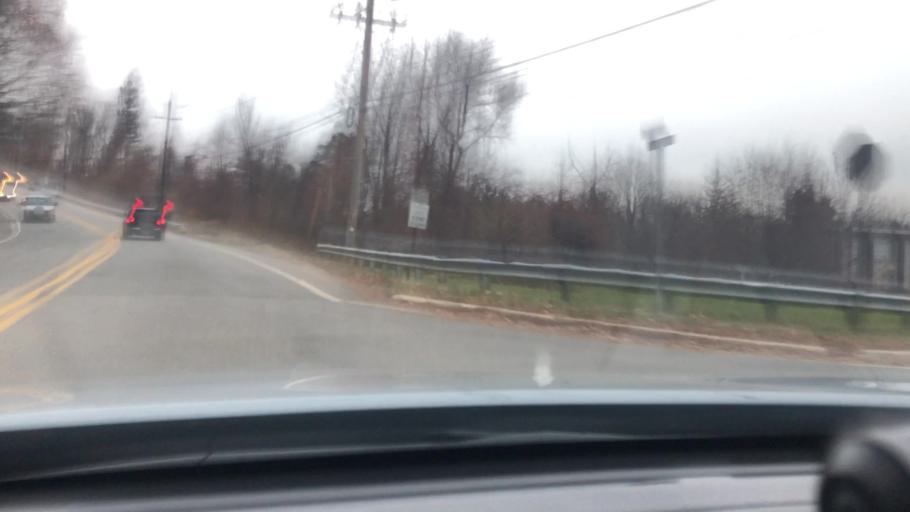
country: US
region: New Jersey
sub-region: Bergen County
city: Woodcliff Lake
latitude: 41.0119
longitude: -74.0692
